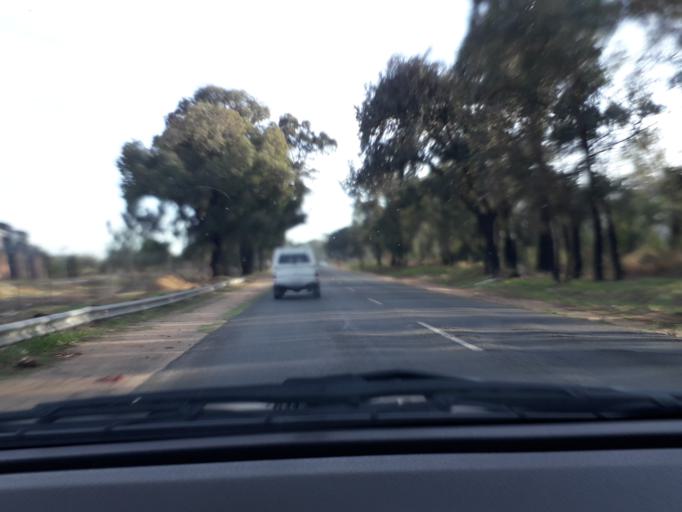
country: ZA
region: Gauteng
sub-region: City of Tshwane Metropolitan Municipality
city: Centurion
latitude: -25.9151
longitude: 28.1578
